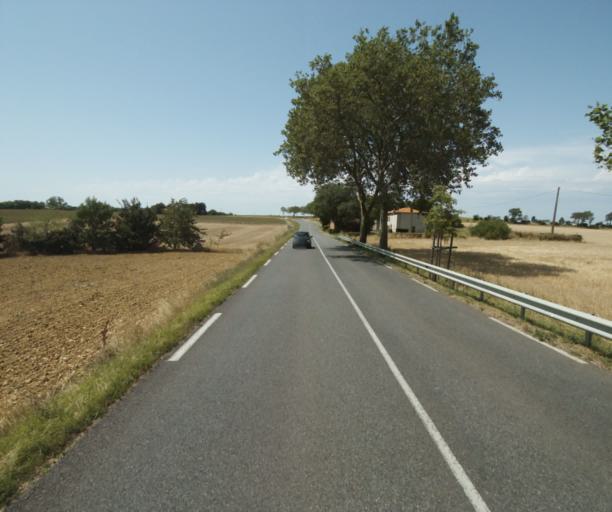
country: FR
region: Midi-Pyrenees
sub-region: Departement de la Haute-Garonne
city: Saint-Felix-Lauragais
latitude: 43.4610
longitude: 1.8432
